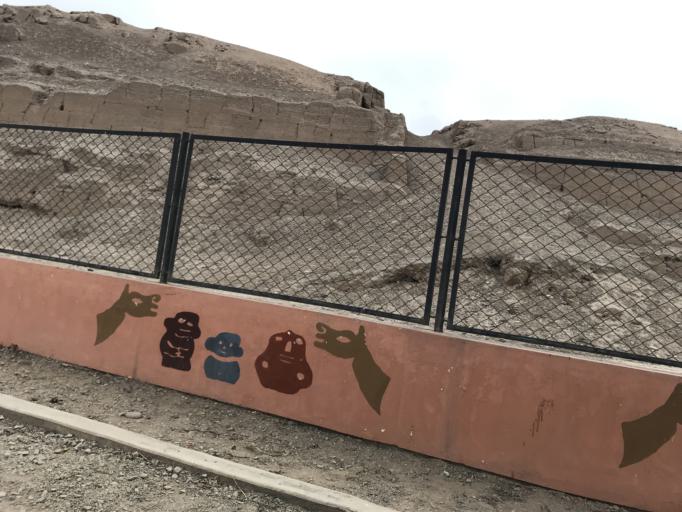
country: PE
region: Callao
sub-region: Callao
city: Callao
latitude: -12.0719
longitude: -77.0842
